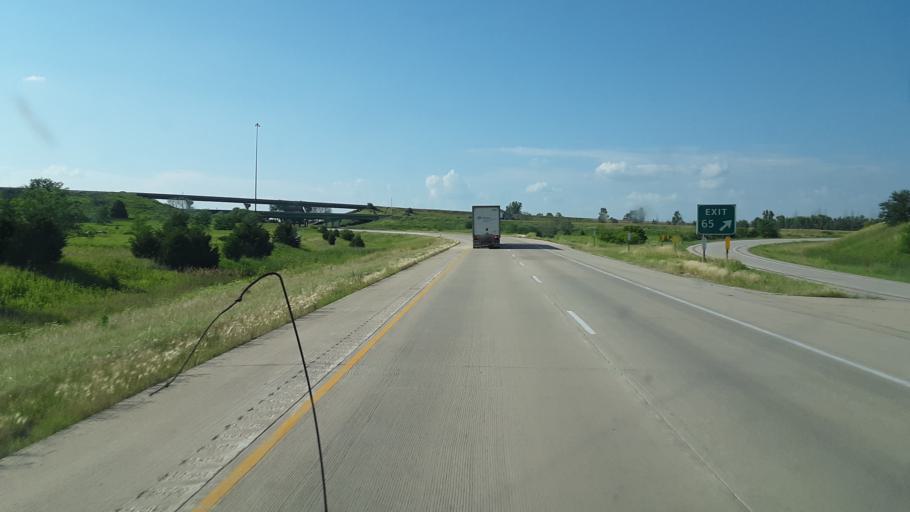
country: US
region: Iowa
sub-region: Black Hawk County
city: Elk Run Heights
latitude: 42.4456
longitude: -92.1893
